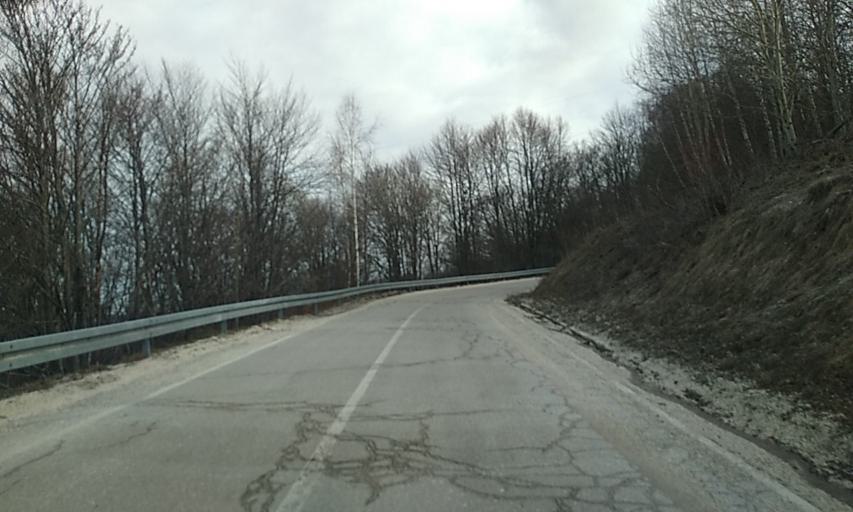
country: RS
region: Central Serbia
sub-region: Jablanicki Okrug
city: Crna Trava
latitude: 42.6782
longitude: 22.3717
